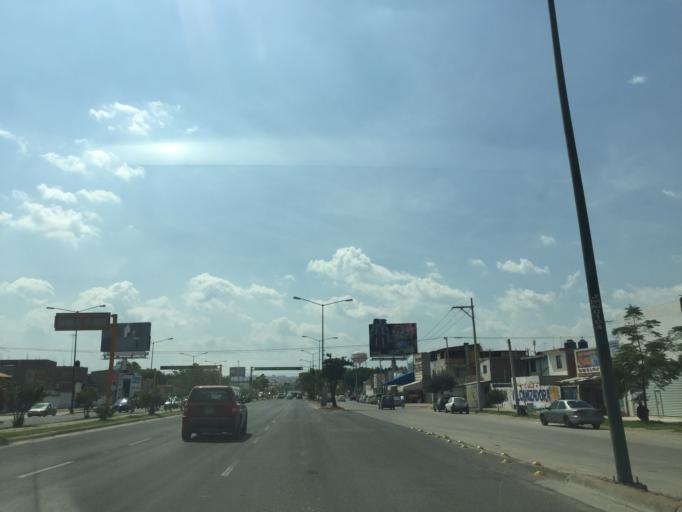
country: MX
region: Guanajuato
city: Leon
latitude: 21.1735
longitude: -101.6646
